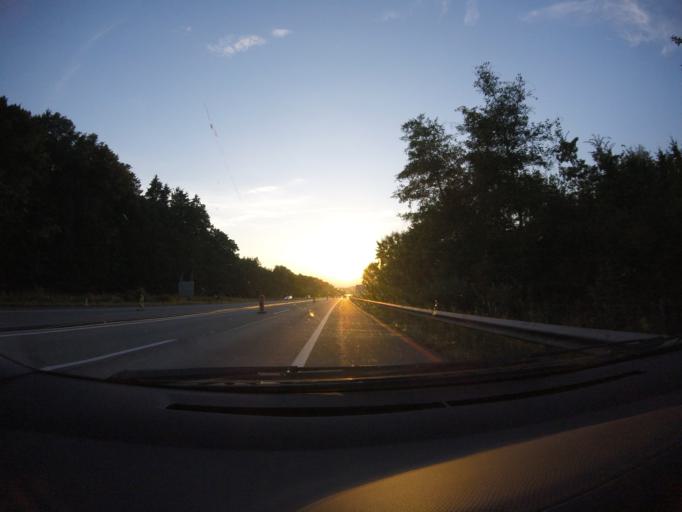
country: AT
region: Styria
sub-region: Politischer Bezirk Weiz
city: Sinabelkirchen
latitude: 47.0926
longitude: 15.8344
